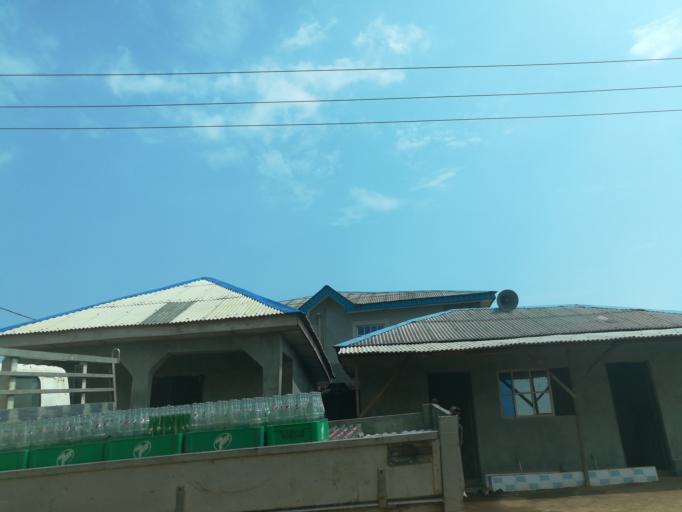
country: NG
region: Lagos
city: Ikorodu
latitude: 6.6009
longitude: 3.6266
